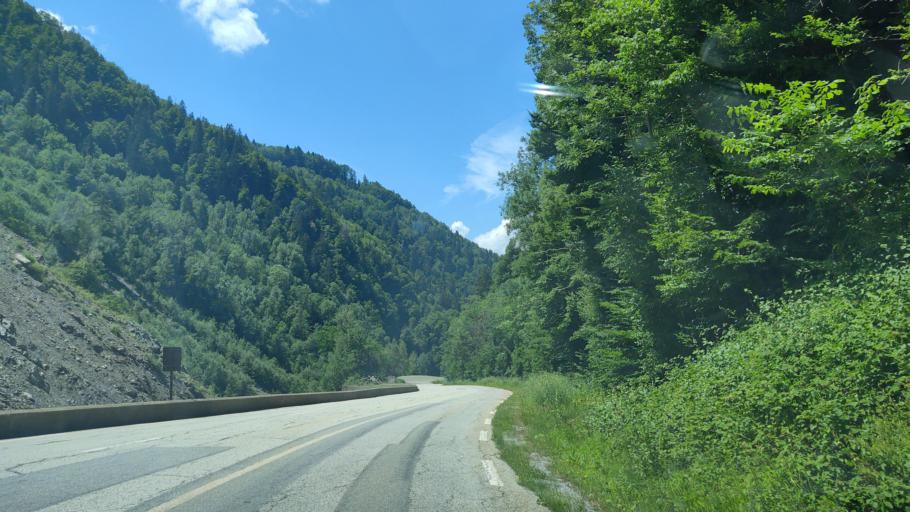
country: FR
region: Rhone-Alpes
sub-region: Departement de la Savoie
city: Ugine
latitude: 45.7569
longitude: 6.4704
